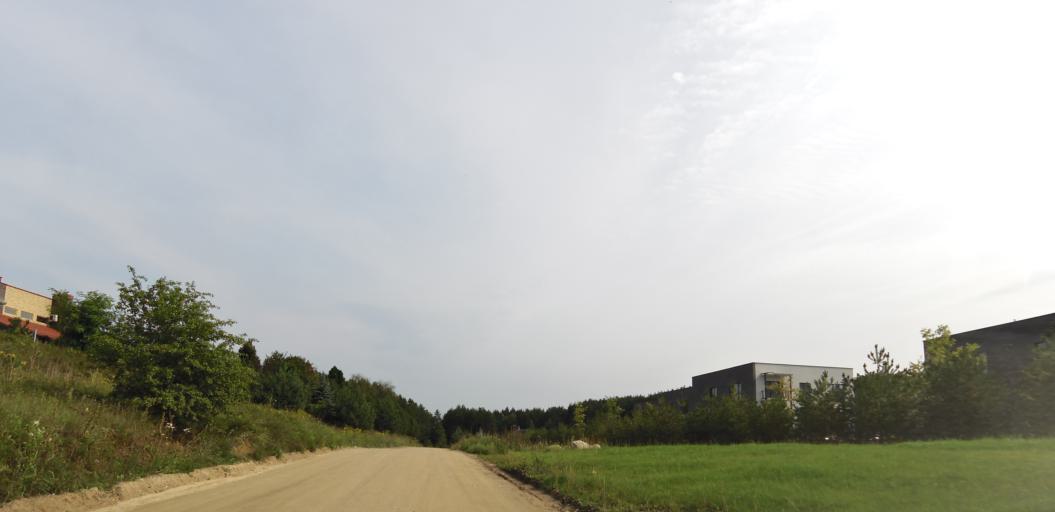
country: LT
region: Vilnius County
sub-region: Vilnius
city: Fabijoniskes
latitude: 54.7495
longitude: 25.2322
